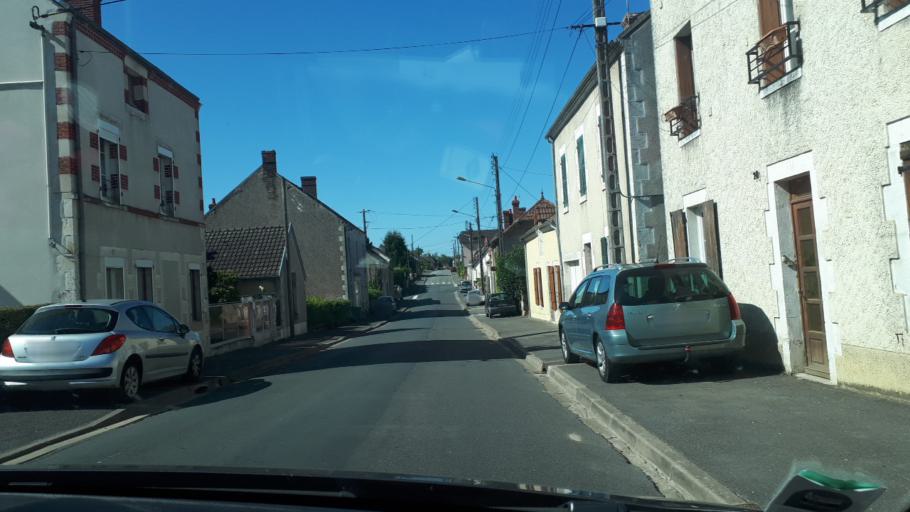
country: FR
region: Centre
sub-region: Departement du Loiret
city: Briare
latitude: 47.5887
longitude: 2.7431
